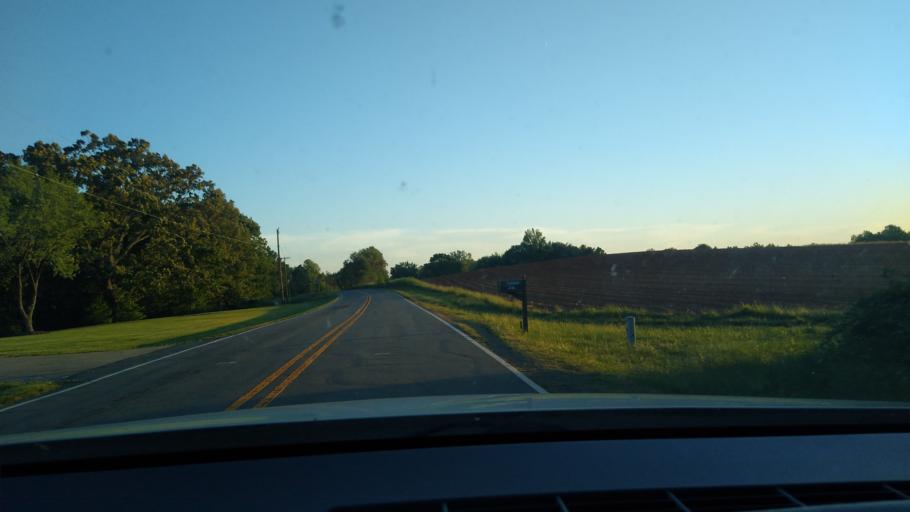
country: US
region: North Carolina
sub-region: Rockingham County
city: Reidsville
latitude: 36.3465
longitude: -79.5708
